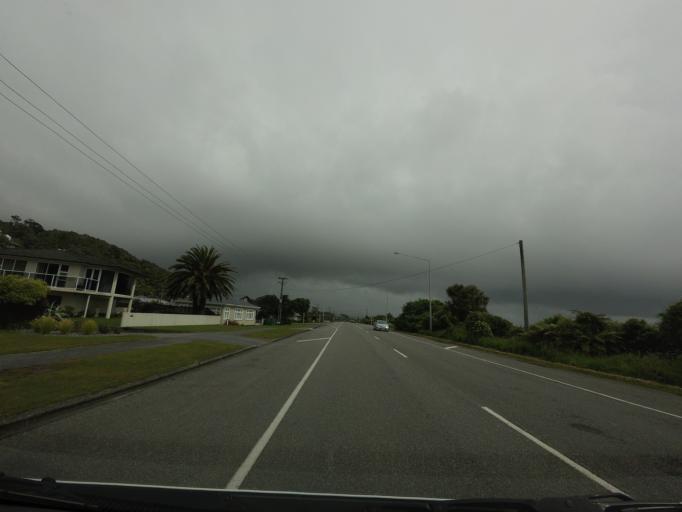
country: NZ
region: West Coast
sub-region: Grey District
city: Greymouth
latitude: -42.4820
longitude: 171.1834
